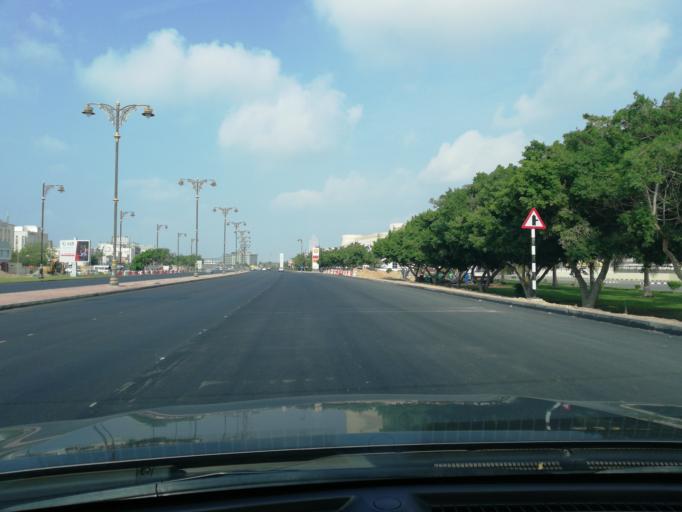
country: OM
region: Zufar
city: Salalah
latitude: 17.0227
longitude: 54.0692
